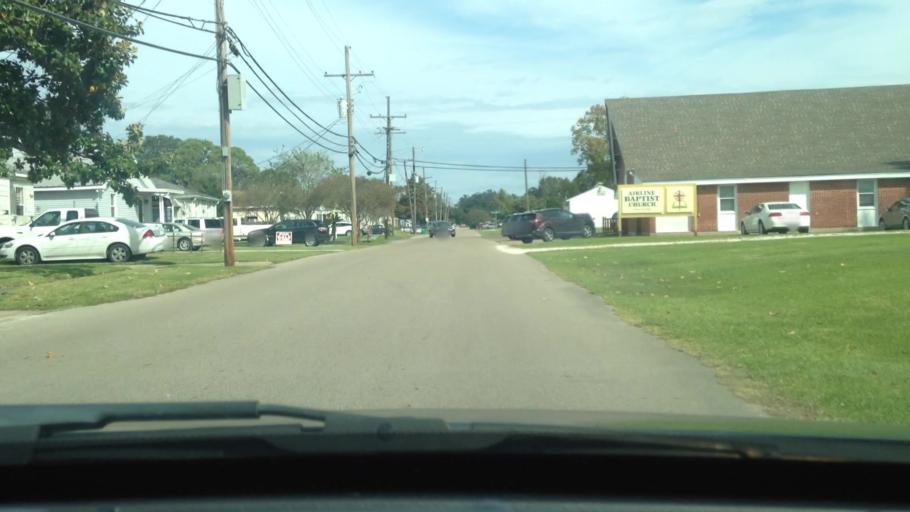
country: US
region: Louisiana
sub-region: Jefferson Parish
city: River Ridge
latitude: 29.9813
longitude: -90.2186
